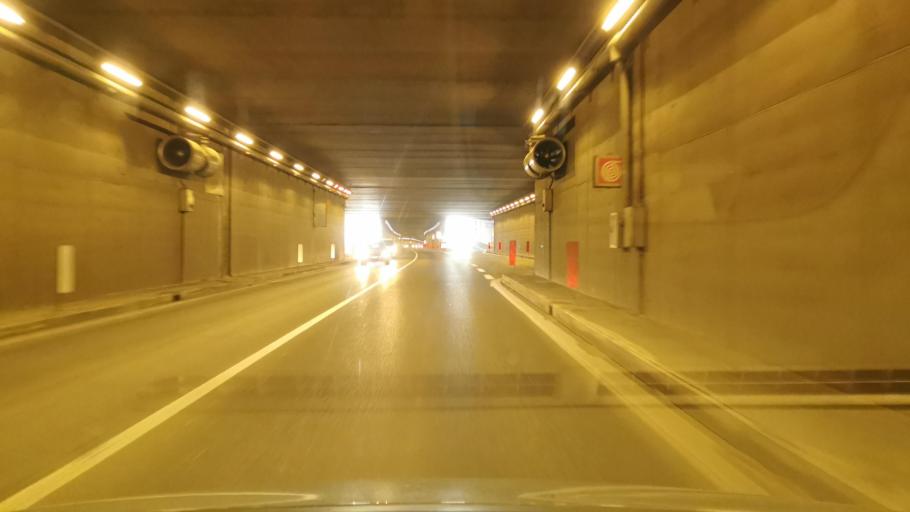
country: IT
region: Piedmont
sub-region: Provincia di Cuneo
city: Cuneo
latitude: 44.3751
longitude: 7.5389
